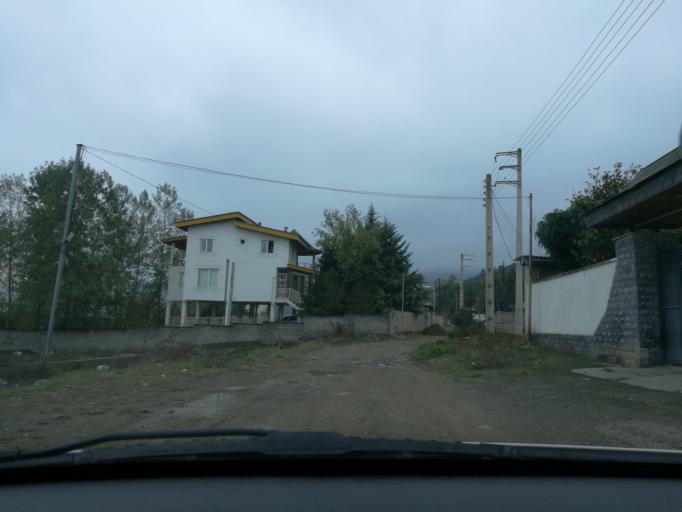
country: IR
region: Mazandaran
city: `Abbasabad
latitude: 36.5052
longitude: 51.1987
